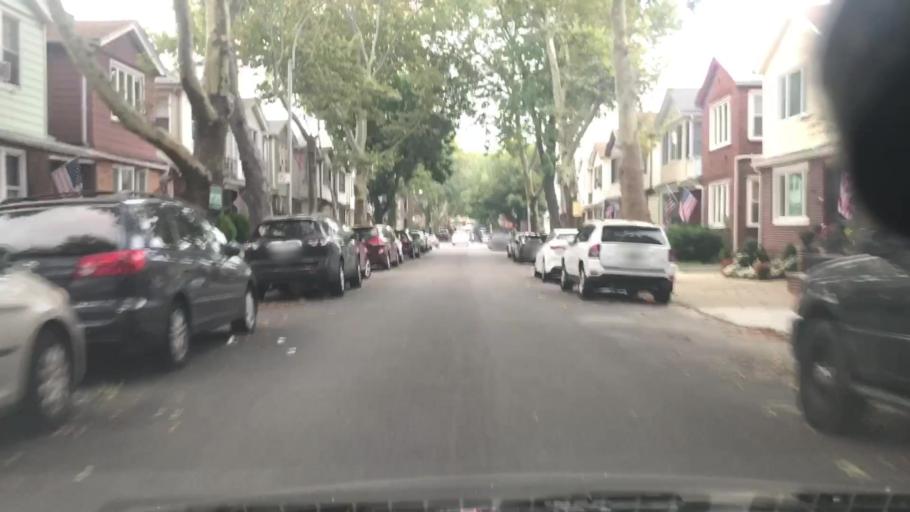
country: US
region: New York
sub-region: Kings County
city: East New York
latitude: 40.7042
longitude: -73.8877
